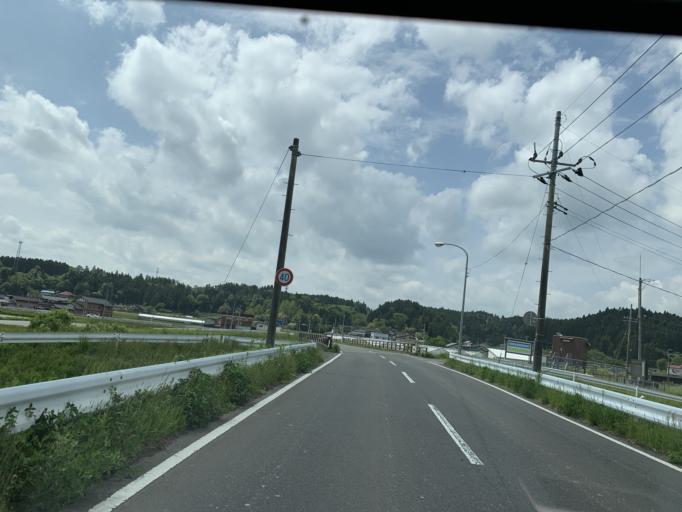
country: JP
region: Miyagi
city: Furukawa
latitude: 38.7430
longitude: 140.9316
